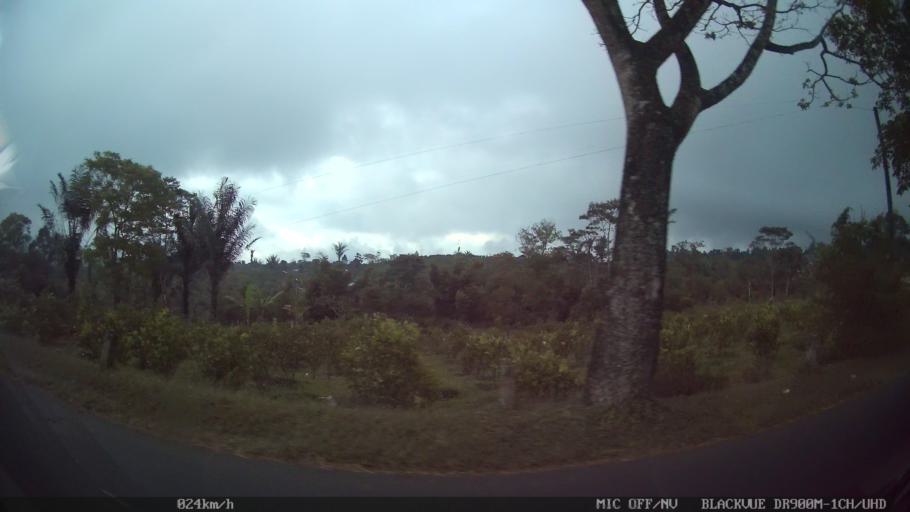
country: ID
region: Bali
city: Banjar Kedisan
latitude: -8.2659
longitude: 115.3313
